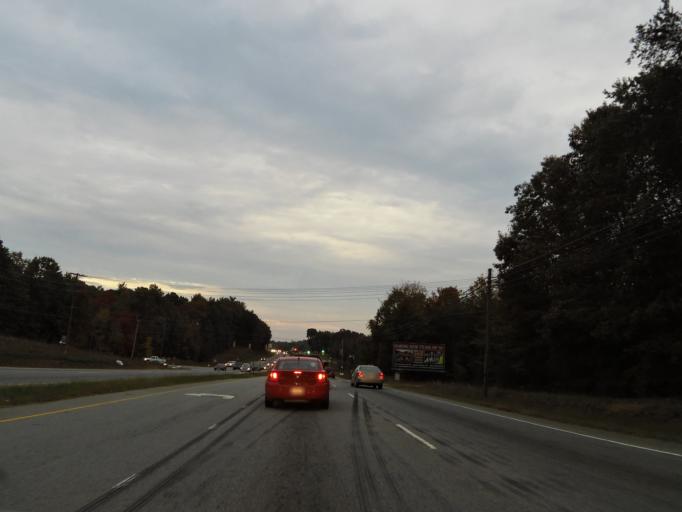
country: US
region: North Carolina
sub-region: Caldwell County
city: Northlakes
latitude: 35.7638
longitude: -81.3835
